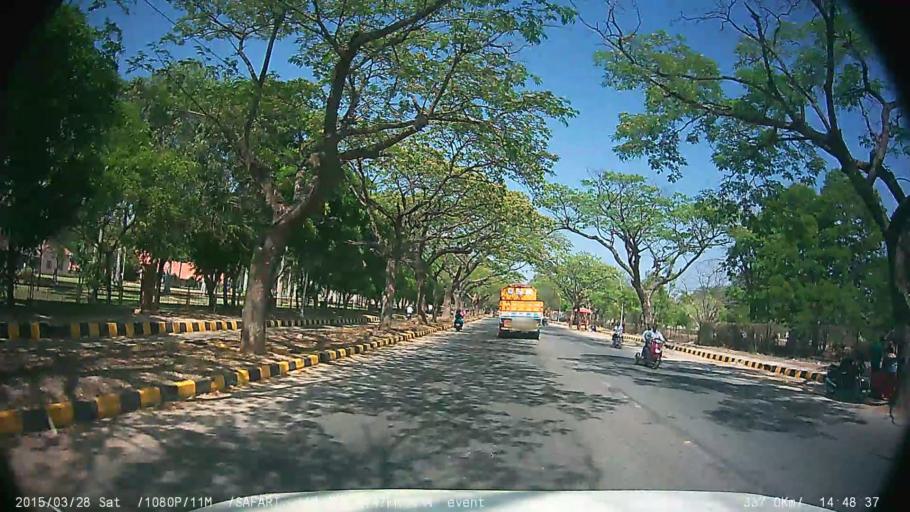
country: IN
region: Karnataka
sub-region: Mysore
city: Mysore
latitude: 12.2980
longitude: 76.6729
